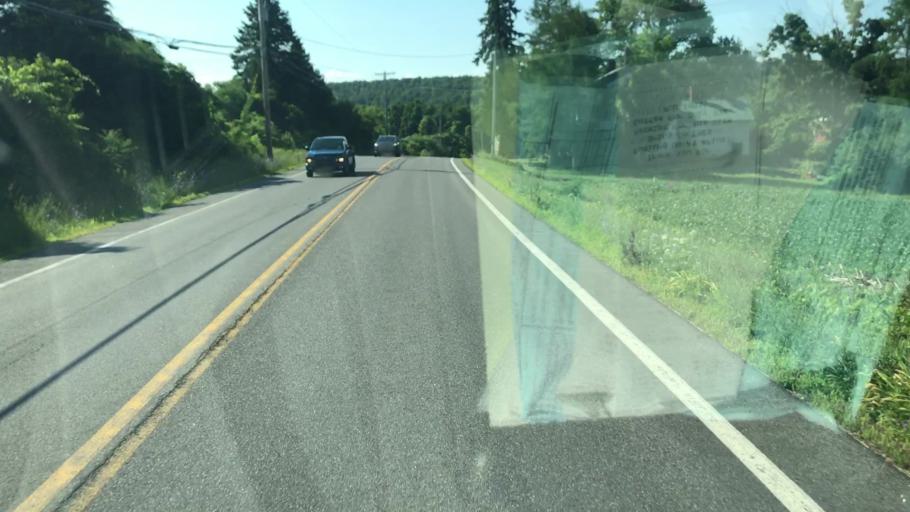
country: US
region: New York
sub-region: Onondaga County
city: Marcellus
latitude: 43.0281
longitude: -76.3621
